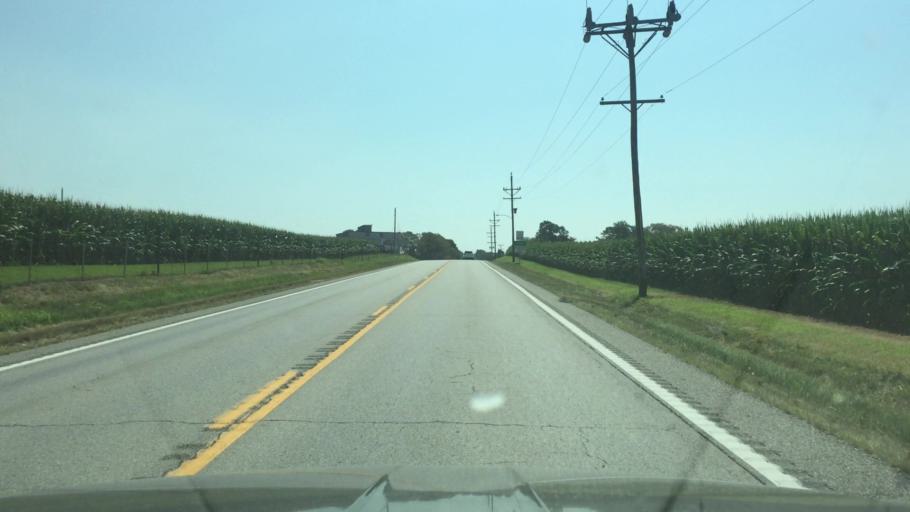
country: US
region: Missouri
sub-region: Moniteau County
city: Tipton
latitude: 38.6697
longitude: -92.8866
